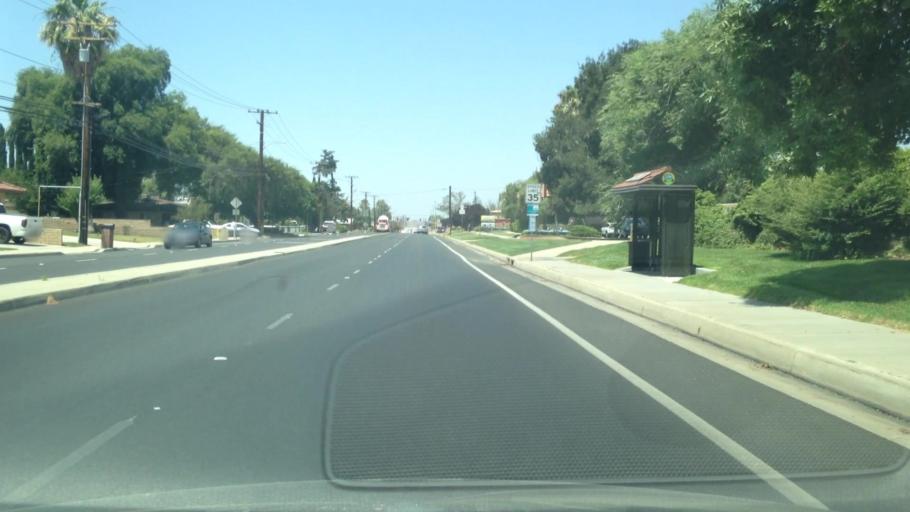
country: US
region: California
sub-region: Riverside County
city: Beaumont
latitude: 33.9471
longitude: -116.9721
